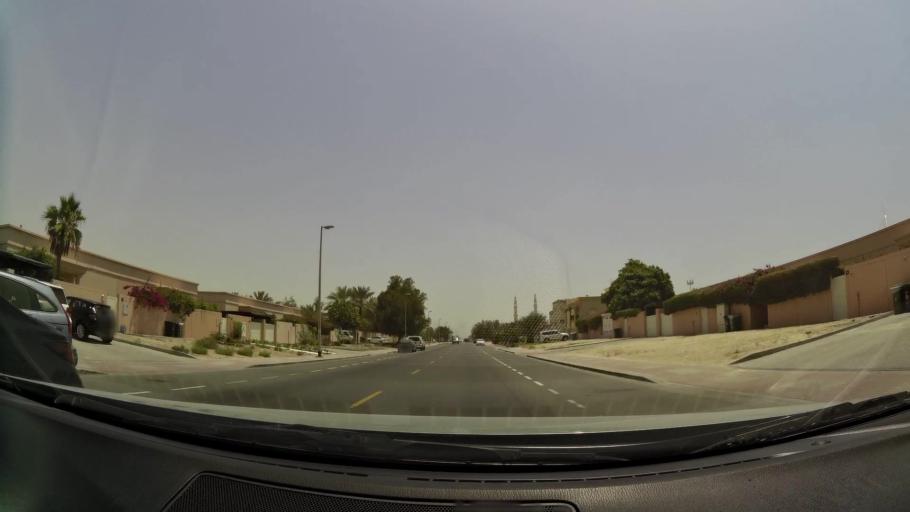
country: AE
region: Dubai
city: Dubai
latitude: 25.1409
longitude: 55.2009
